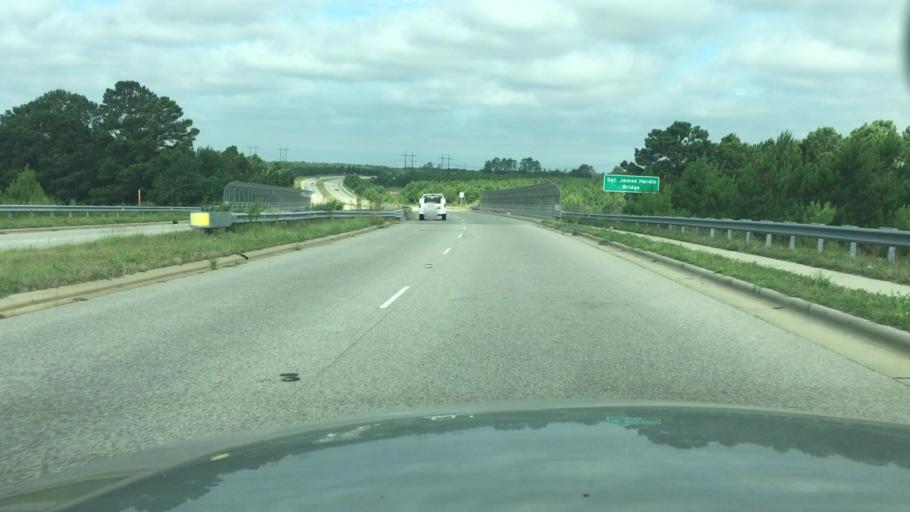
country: US
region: North Carolina
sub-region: Cumberland County
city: Hope Mills
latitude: 34.9901
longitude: -78.9401
